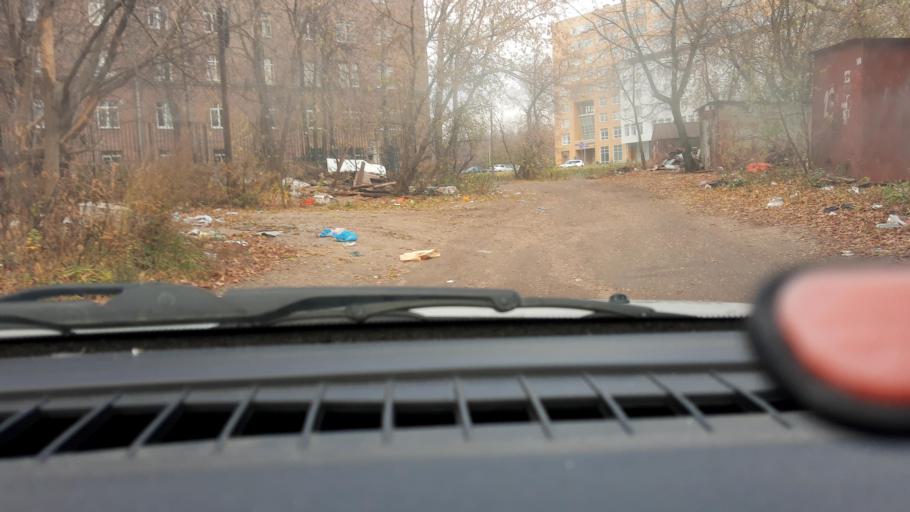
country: RU
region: Nizjnij Novgorod
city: Nizhniy Novgorod
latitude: 56.2975
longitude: 43.9773
